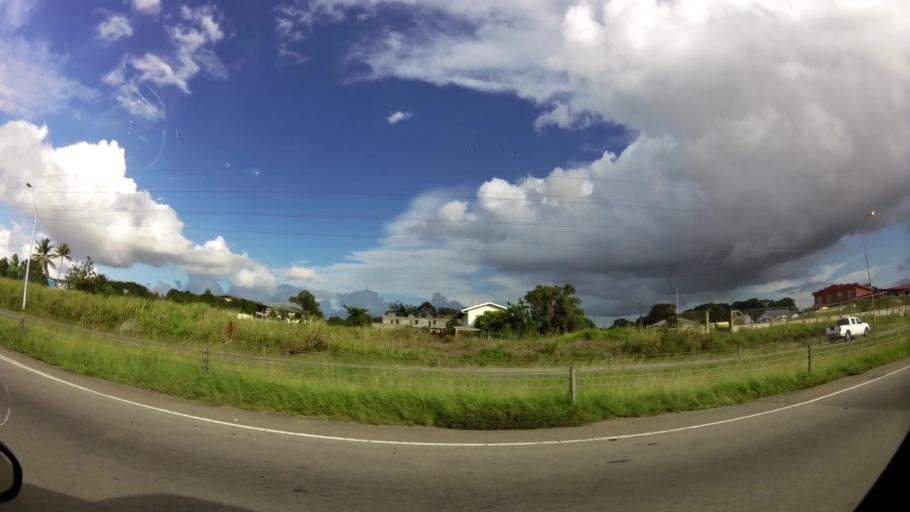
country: TT
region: Couva-Tabaquite-Talparo
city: Couva
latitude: 10.4523
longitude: -61.4107
